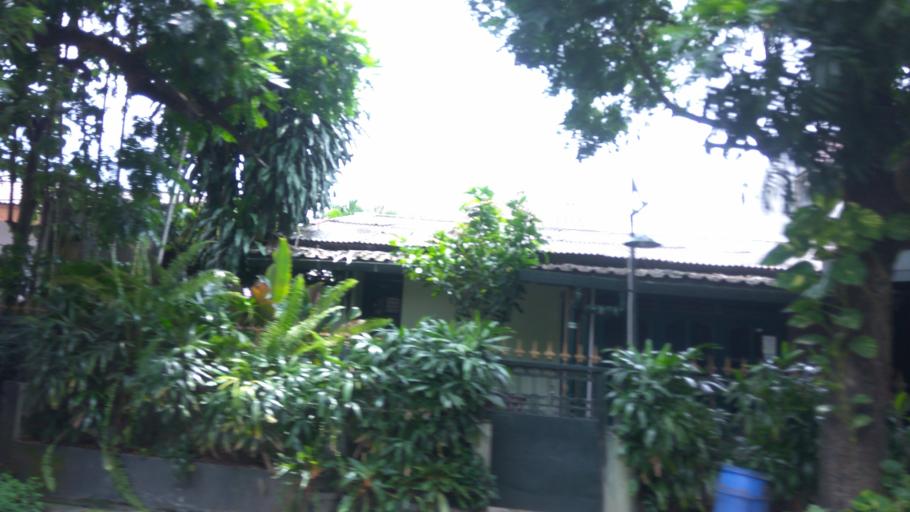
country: ID
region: Daerah Istimewa Yogyakarta
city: Depok
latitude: -7.7411
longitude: 110.4082
